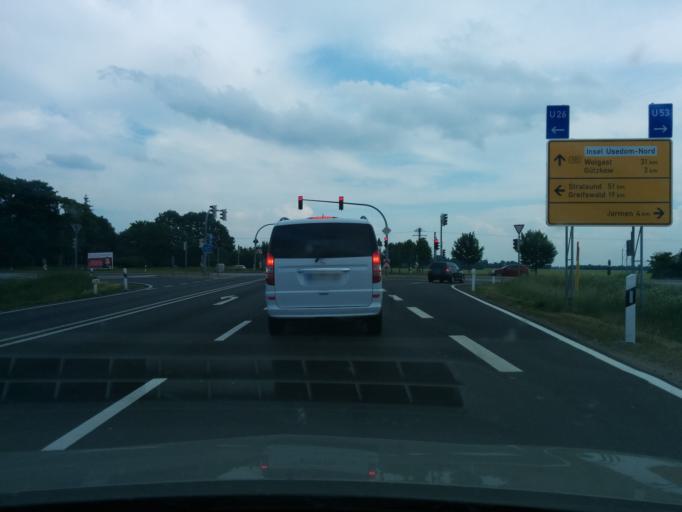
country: DE
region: Mecklenburg-Vorpommern
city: Jarmen
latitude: 53.9468
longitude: 13.3740
